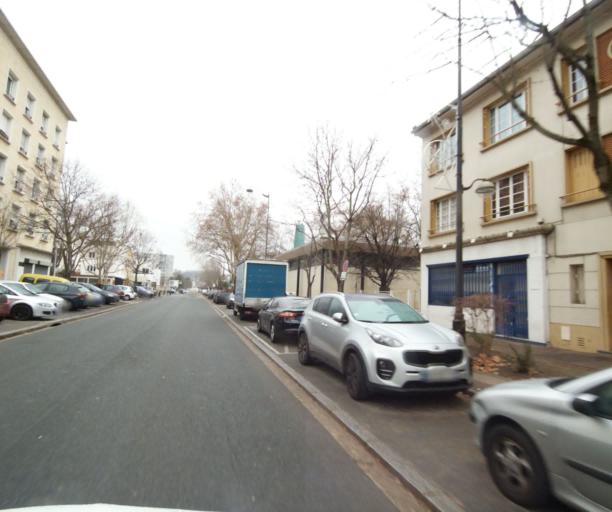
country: FR
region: Ile-de-France
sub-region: Departement des Hauts-de-Seine
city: Rueil-Malmaison
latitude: 48.8889
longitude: 2.1831
